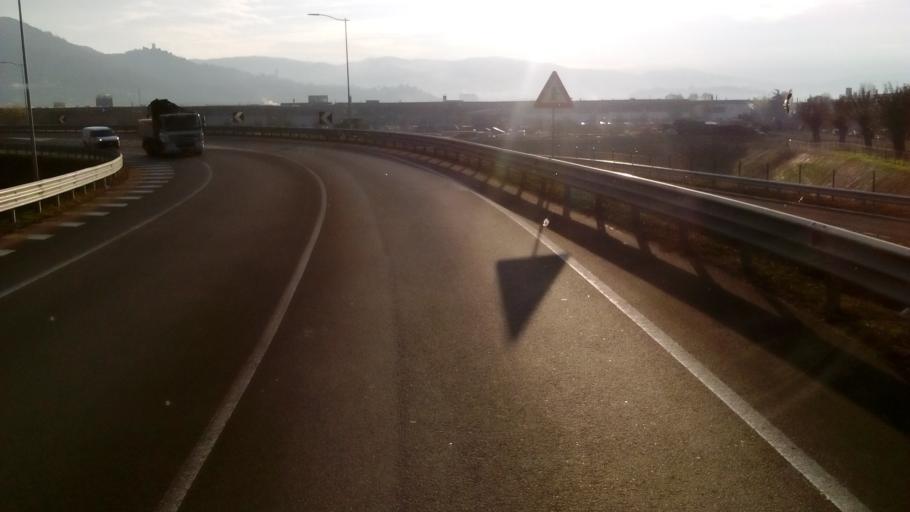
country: IT
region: Veneto
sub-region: Provincia di Vicenza
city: Brendola
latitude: 45.4852
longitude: 11.4274
